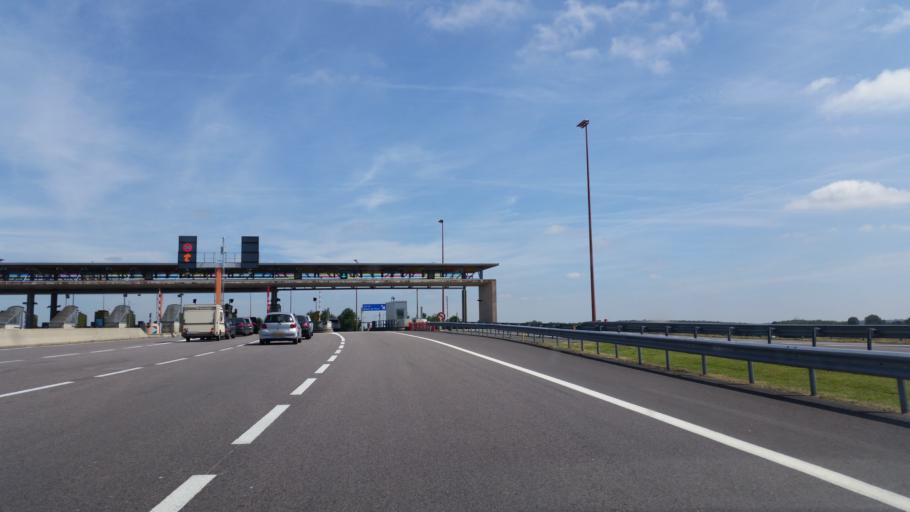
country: FR
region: Haute-Normandie
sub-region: Departement de la Seine-Maritime
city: Aumale
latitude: 49.7588
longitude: 1.7020
